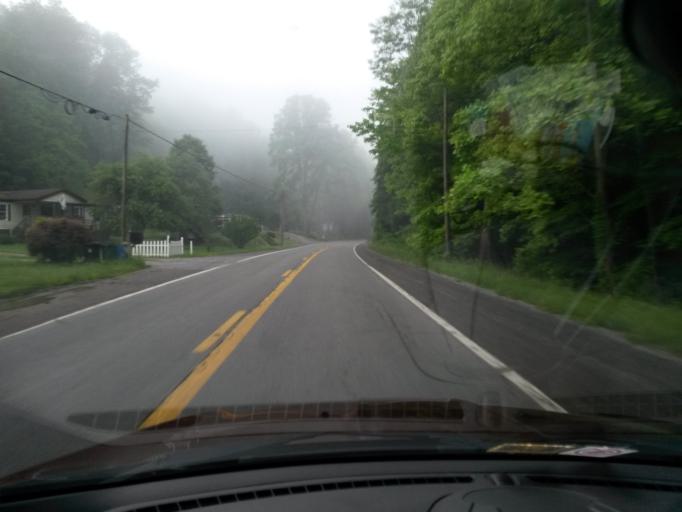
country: US
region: West Virginia
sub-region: McDowell County
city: Welch
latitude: 37.4631
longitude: -81.5409
